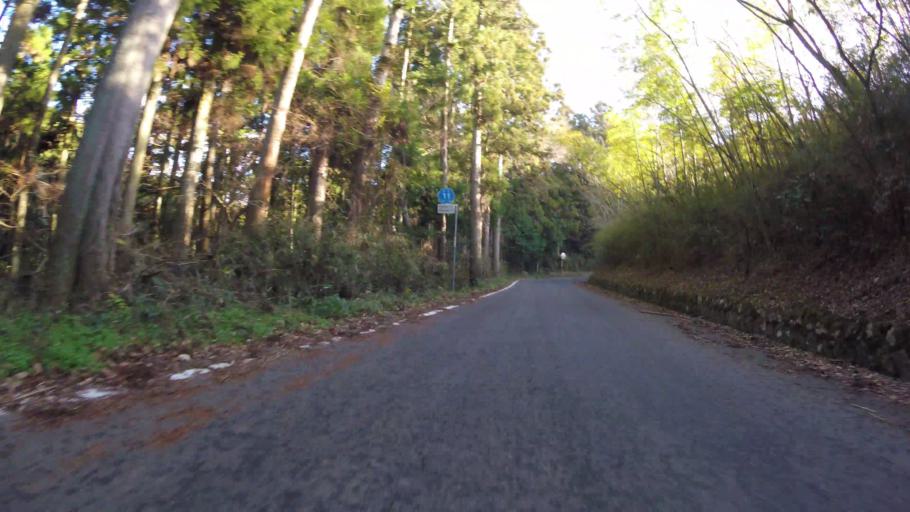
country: JP
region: Kanagawa
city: Yugawara
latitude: 35.1215
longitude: 139.0172
